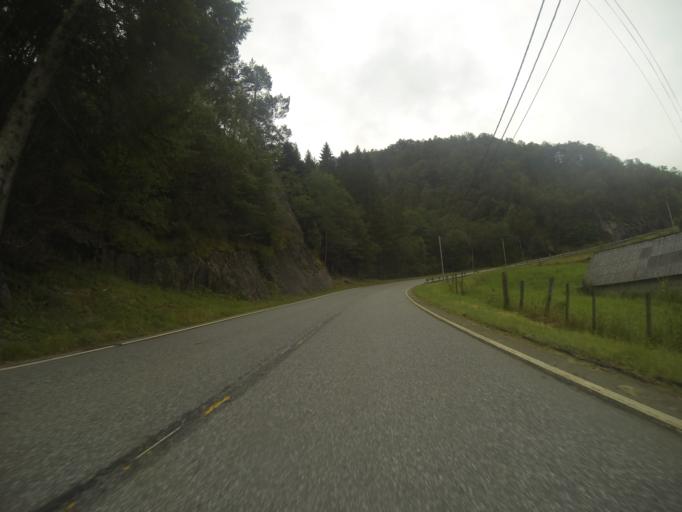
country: NO
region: Rogaland
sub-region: Suldal
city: Sand
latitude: 59.4848
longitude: 6.2054
